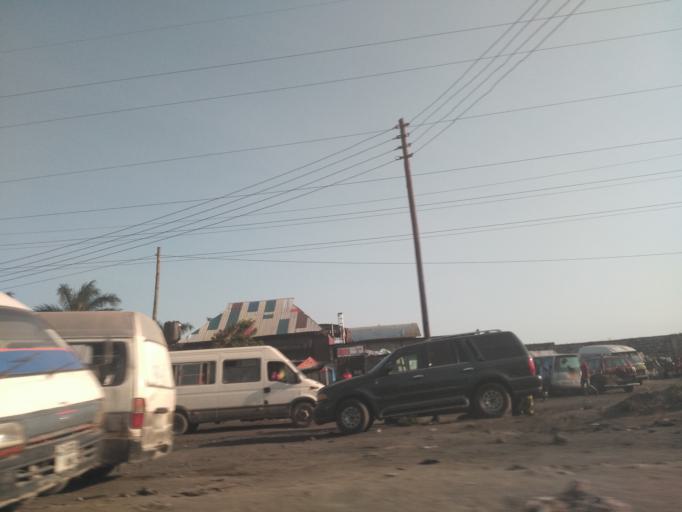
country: TZ
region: Dar es Salaam
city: Dar es Salaam
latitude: -6.9150
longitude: 39.2691
